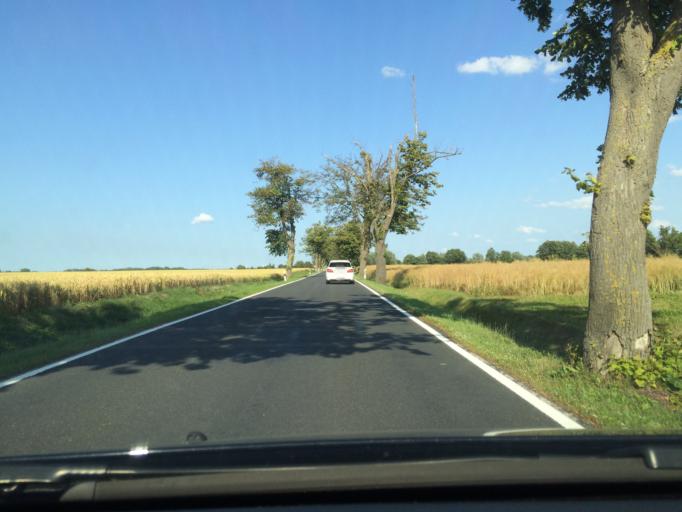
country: DE
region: Mecklenburg-Vorpommern
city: Niepars
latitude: 54.3336
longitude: 12.9101
